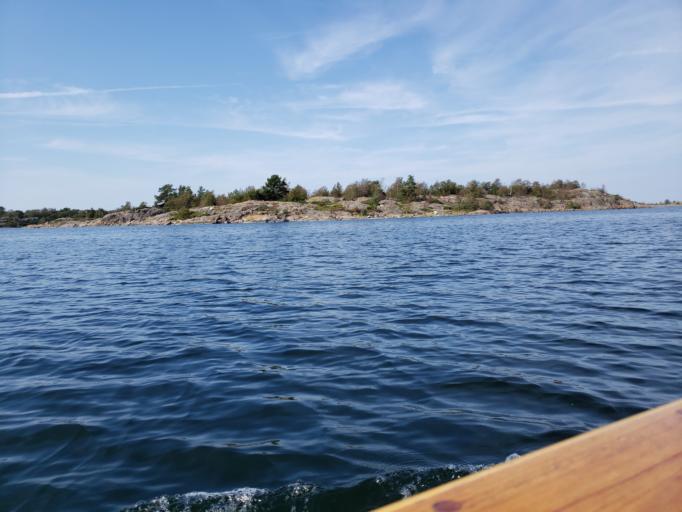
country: FI
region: Varsinais-Suomi
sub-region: Aboland-Turunmaa
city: Dragsfjaerd
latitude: 59.8502
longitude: 22.2115
